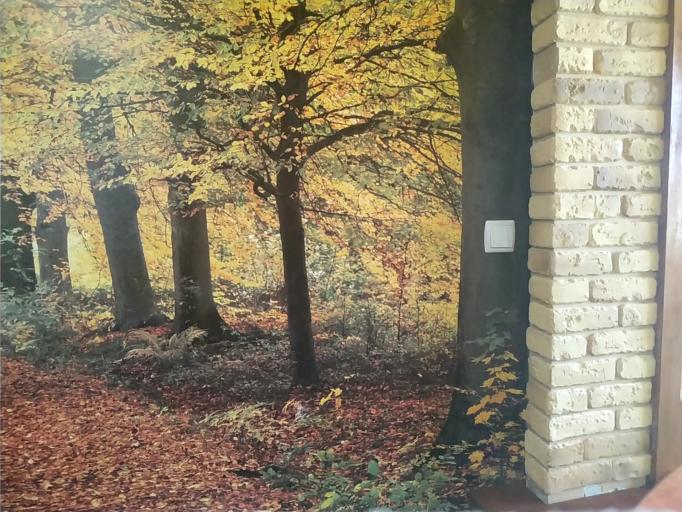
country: RU
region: Tverskaya
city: Krasnomayskiy
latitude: 57.7164
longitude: 34.4774
